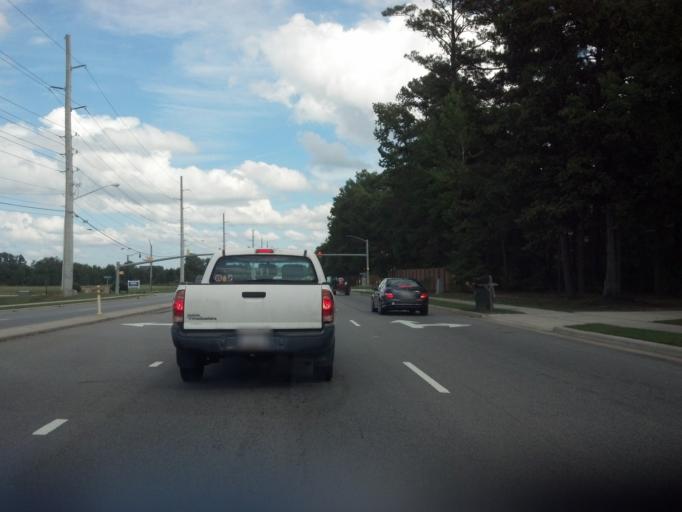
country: US
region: North Carolina
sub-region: Pitt County
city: Windsor
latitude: 35.5527
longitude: -77.3801
